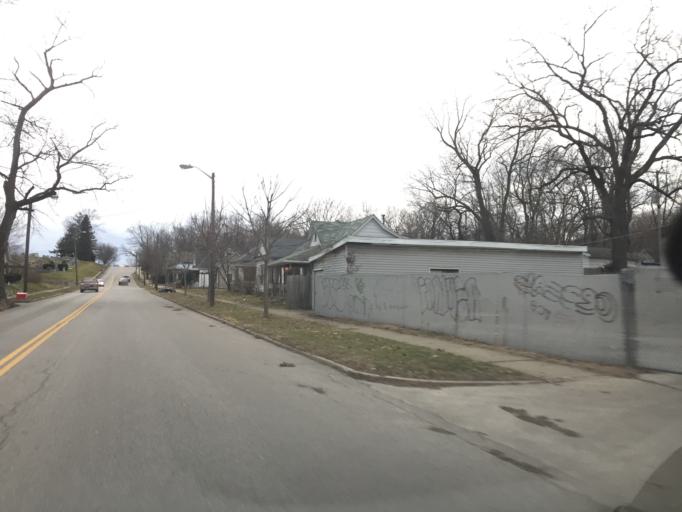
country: US
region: Indiana
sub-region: Monroe County
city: Bloomington
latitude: 39.1666
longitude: -86.5440
